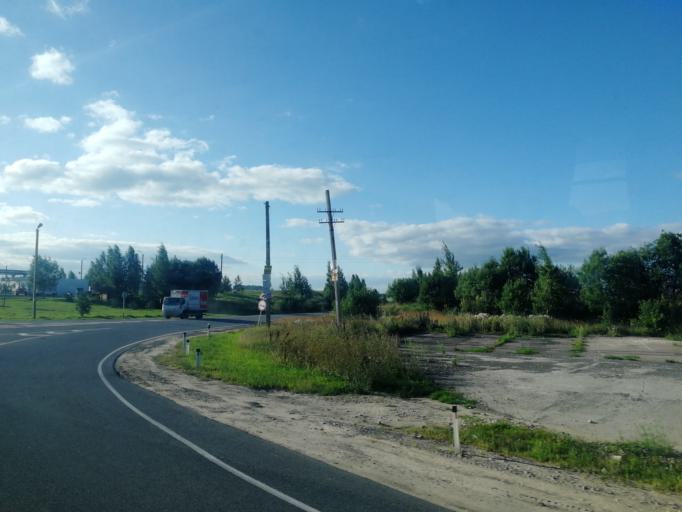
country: RU
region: Tula
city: Dubna
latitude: 54.2821
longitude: 37.1631
